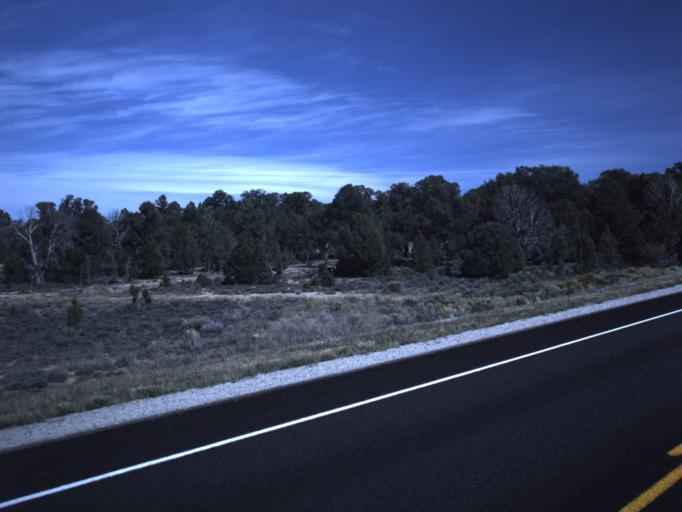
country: US
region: Colorado
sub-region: Dolores County
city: Dove Creek
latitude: 37.8318
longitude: -109.0953
